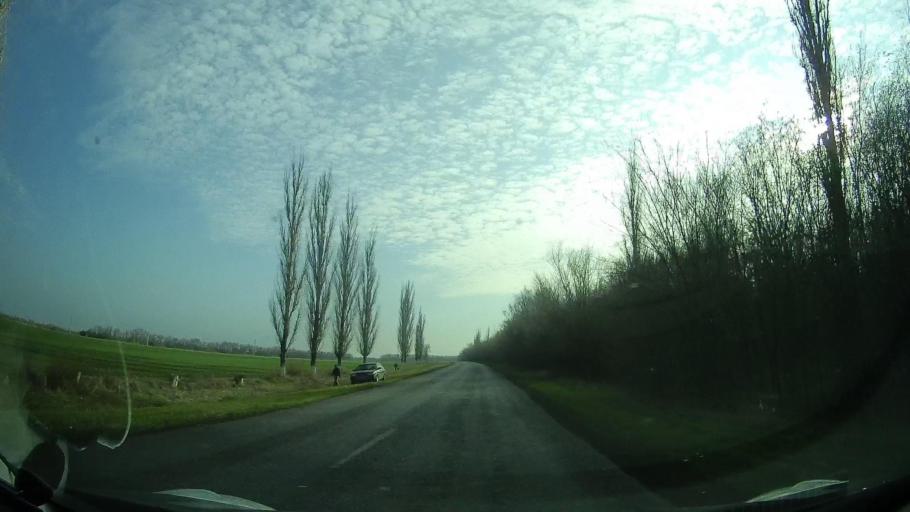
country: RU
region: Rostov
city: Mechetinskaya
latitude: 46.8220
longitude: 40.5547
